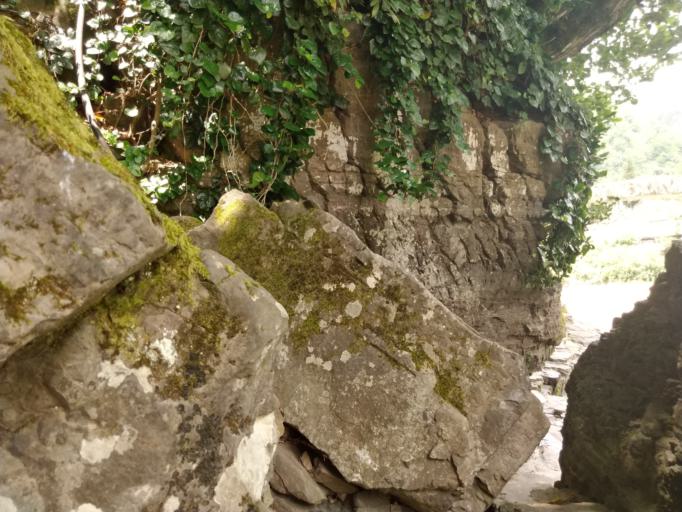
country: GE
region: Ajaria
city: Keda
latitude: 41.5709
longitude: 41.8602
